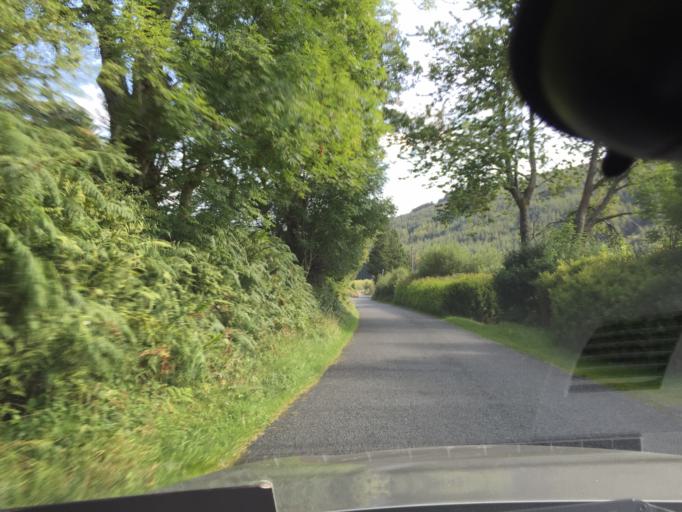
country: IE
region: Leinster
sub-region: Wicklow
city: Rathdrum
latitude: 53.0386
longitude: -6.3240
